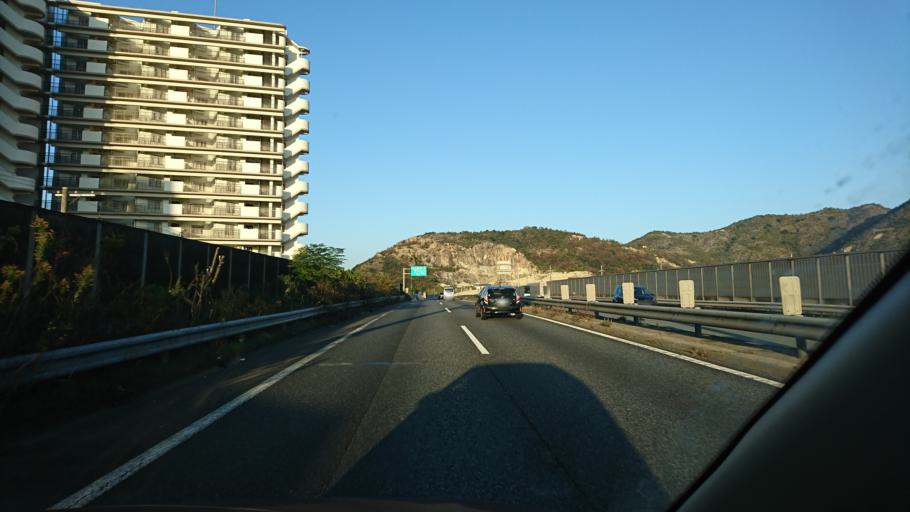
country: JP
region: Hyogo
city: Kakogawacho-honmachi
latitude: 34.7912
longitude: 134.8061
